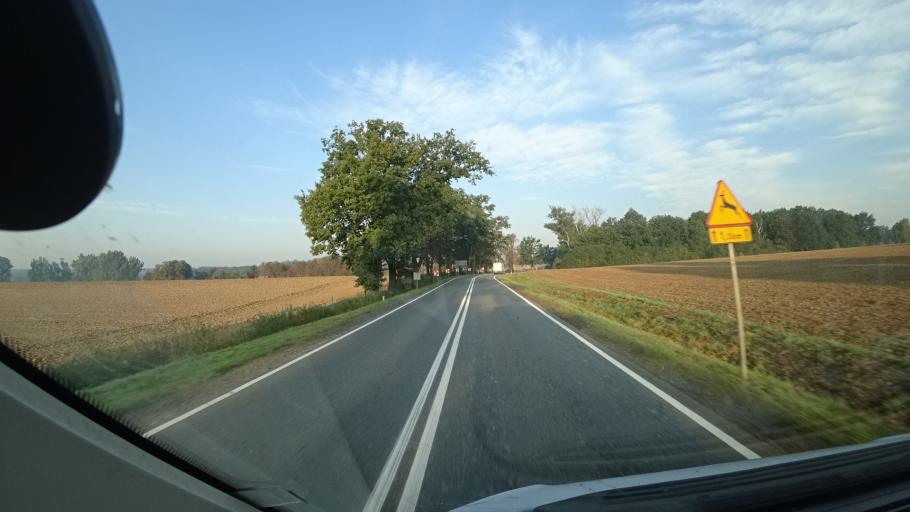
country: PL
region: Silesian Voivodeship
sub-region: Powiat gliwicki
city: Rudziniec
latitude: 50.3866
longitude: 18.4047
